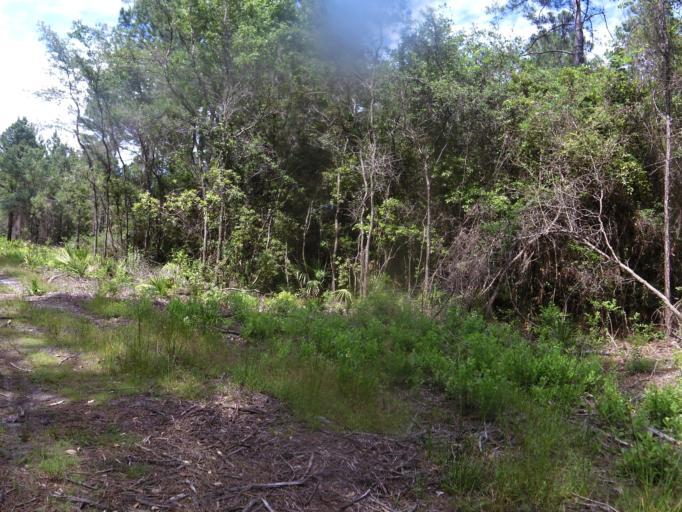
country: US
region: Florida
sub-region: Duval County
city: Atlantic Beach
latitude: 30.4461
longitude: -81.4704
